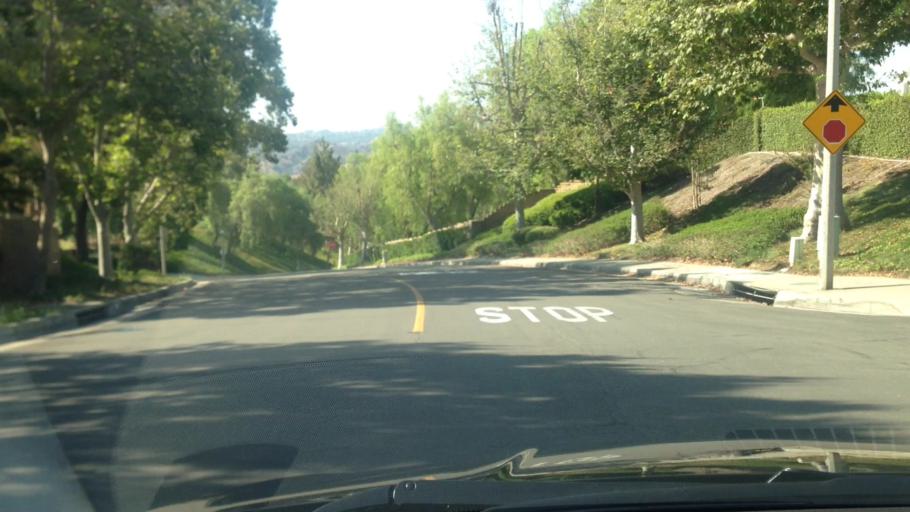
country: US
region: California
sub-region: Orange County
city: Yorba Linda
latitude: 33.8864
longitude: -117.7616
